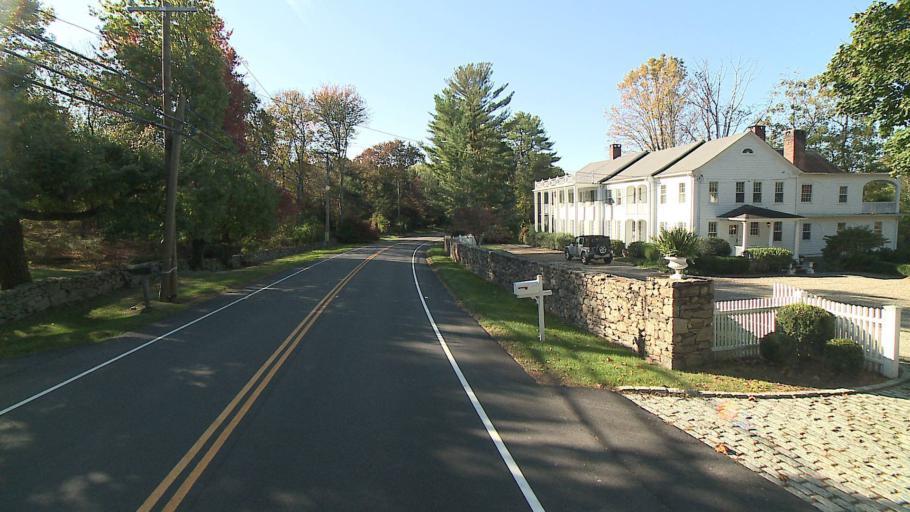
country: US
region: Connecticut
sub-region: Fairfield County
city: Wilton
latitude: 41.1777
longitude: -73.3925
